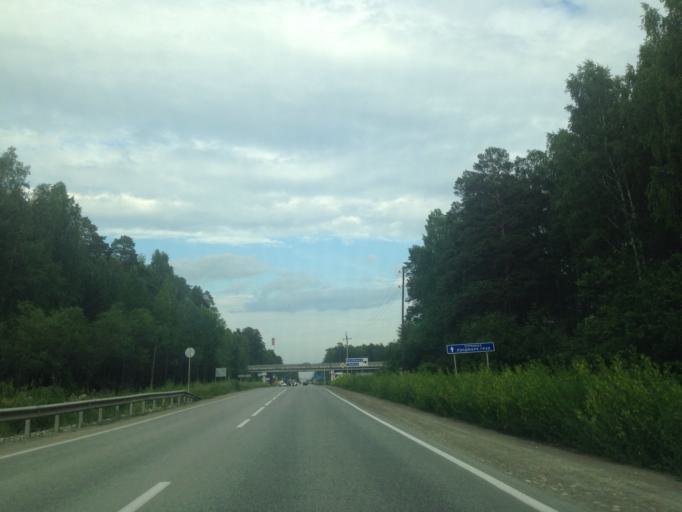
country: RU
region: Sverdlovsk
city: Istok
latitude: 56.8393
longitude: 60.7974
